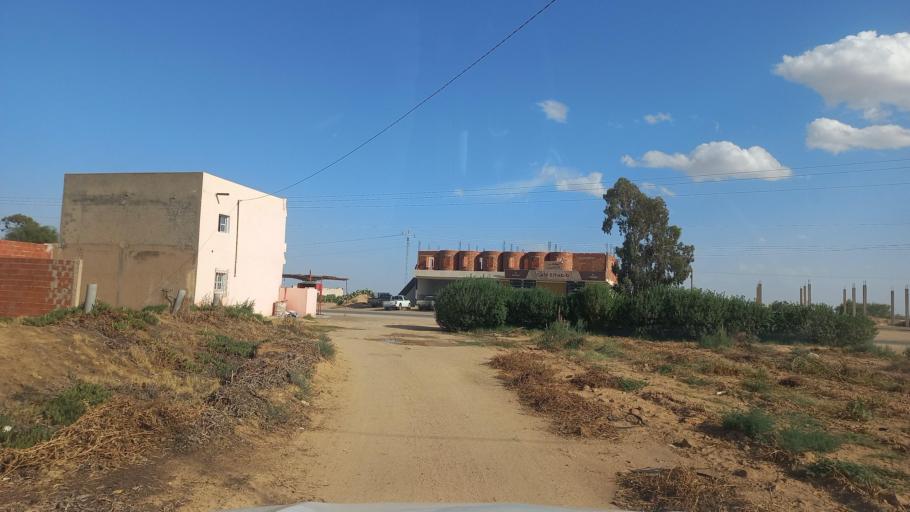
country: TN
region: Al Qasrayn
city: Kasserine
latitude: 35.2576
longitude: 9.0286
